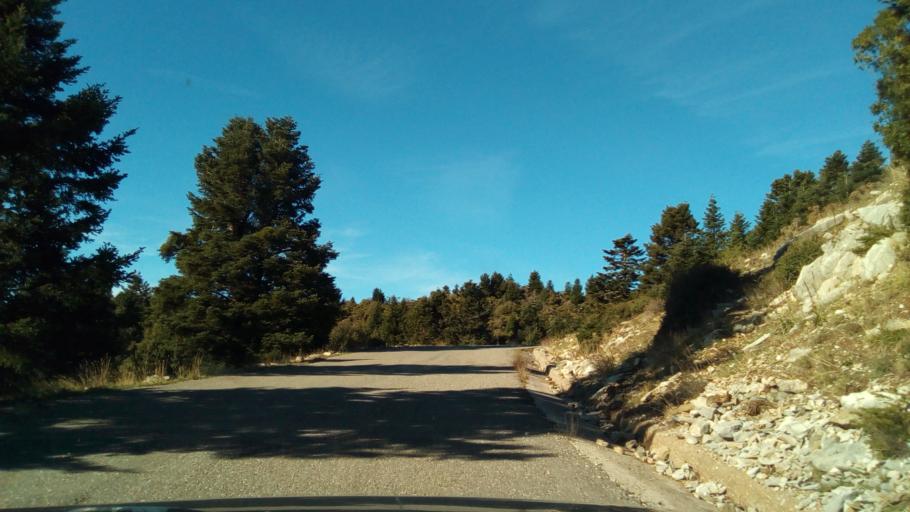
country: GR
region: West Greece
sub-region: Nomos Aitolias kai Akarnanias
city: Nafpaktos
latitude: 38.5296
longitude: 21.8442
